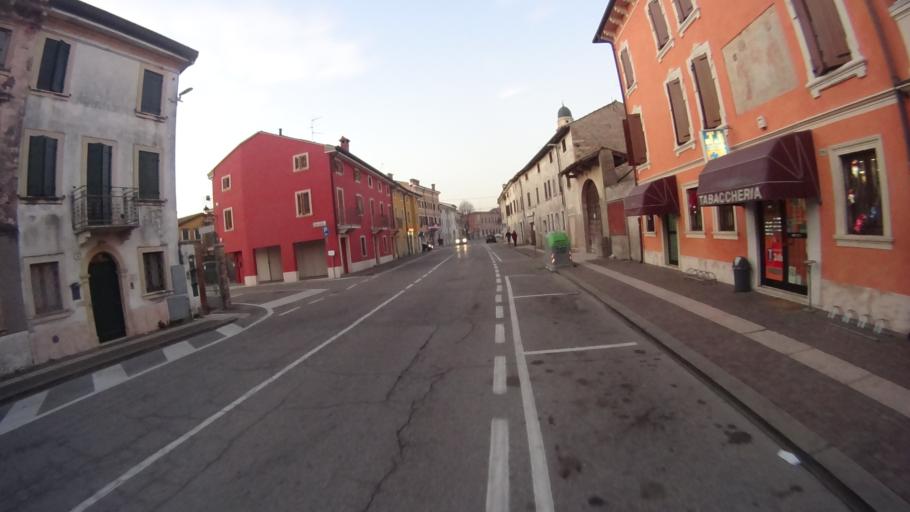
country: IT
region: Veneto
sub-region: Provincia di Verona
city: Povegliano Veronese
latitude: 45.3458
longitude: 10.8816
